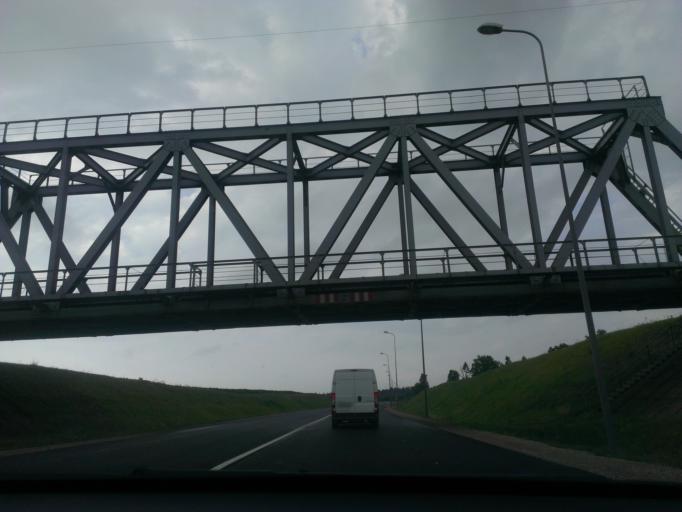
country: LV
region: Lecava
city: Iecava
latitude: 56.6313
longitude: 24.2229
